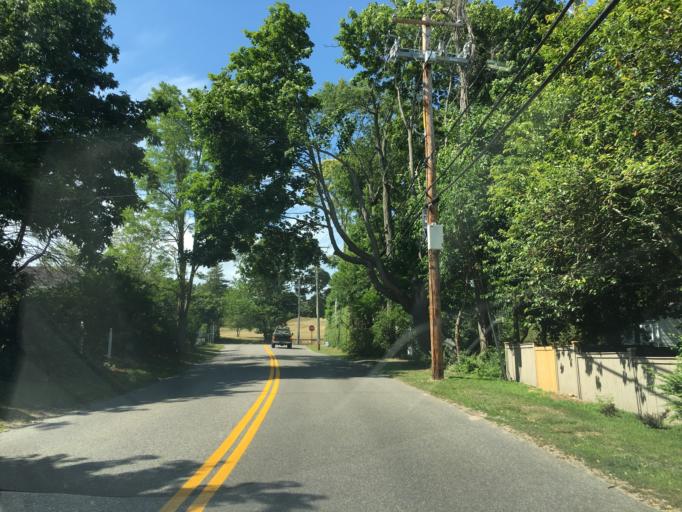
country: US
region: New York
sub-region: Suffolk County
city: Shelter Island Heights
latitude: 41.0736
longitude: -72.3584
